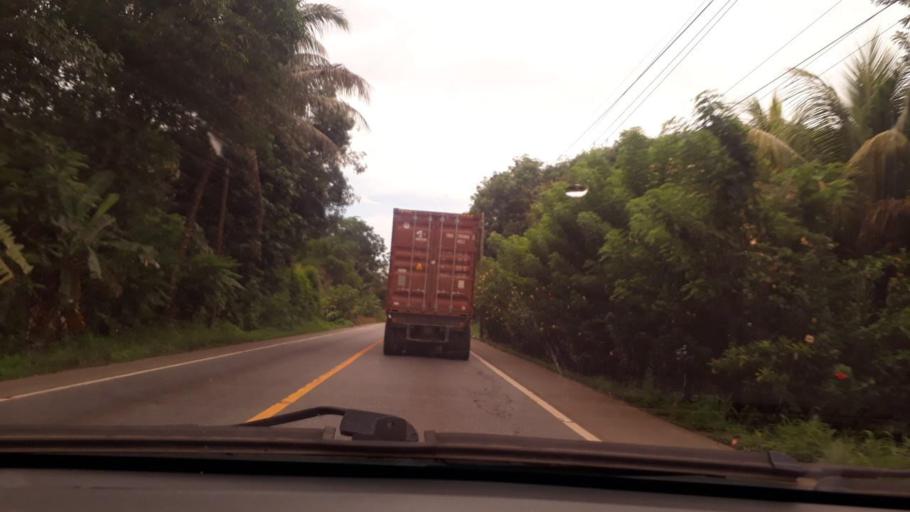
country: GT
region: Izabal
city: Morales
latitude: 15.5566
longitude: -88.6742
